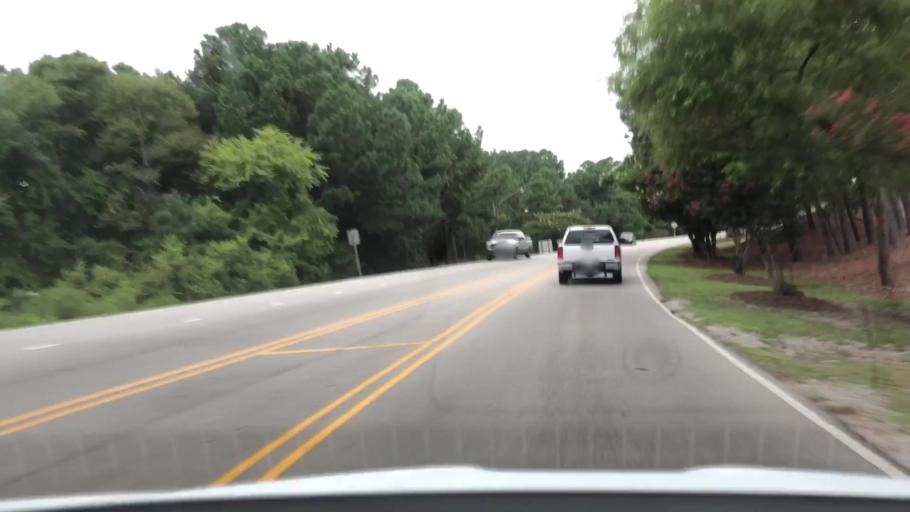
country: US
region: North Carolina
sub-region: Carteret County
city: Cedar Point
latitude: 34.6615
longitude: -77.0606
